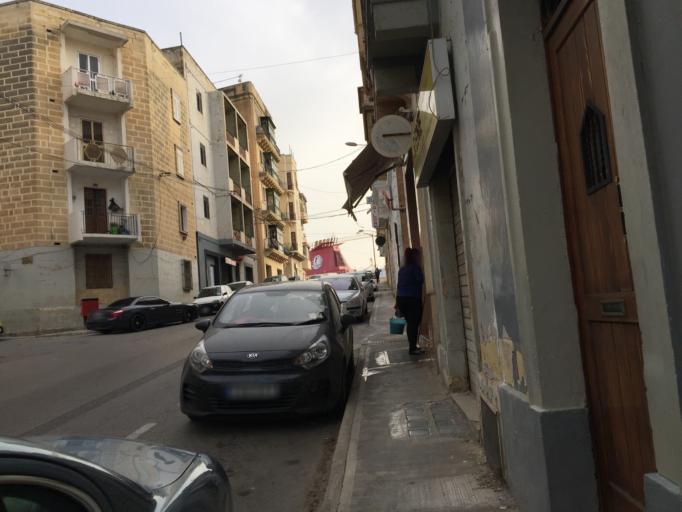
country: MT
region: L-Isla
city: Senglea
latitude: 35.8813
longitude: 14.5187
